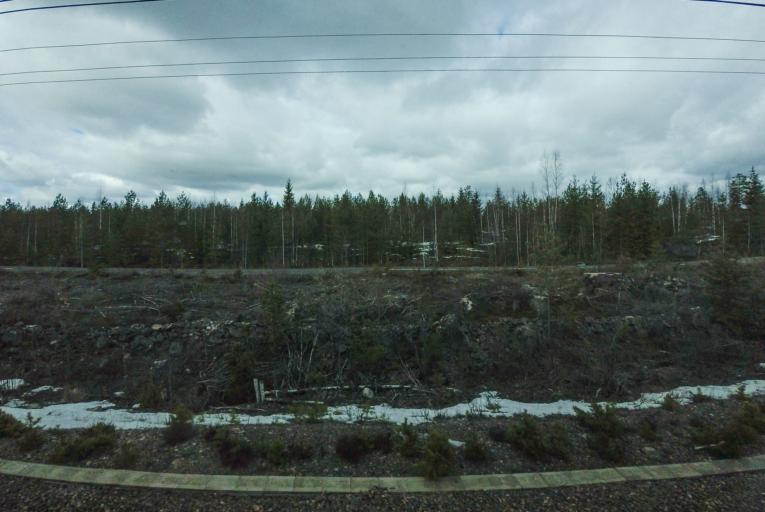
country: FI
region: Paijanne Tavastia
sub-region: Lahti
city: Nastola
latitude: 60.9292
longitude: 26.0670
